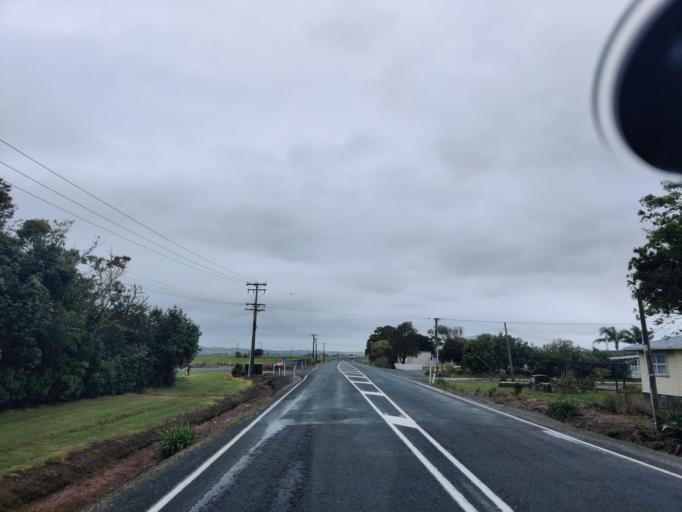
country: NZ
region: Northland
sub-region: Kaipara District
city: Dargaville
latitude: -36.1219
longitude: 174.0103
